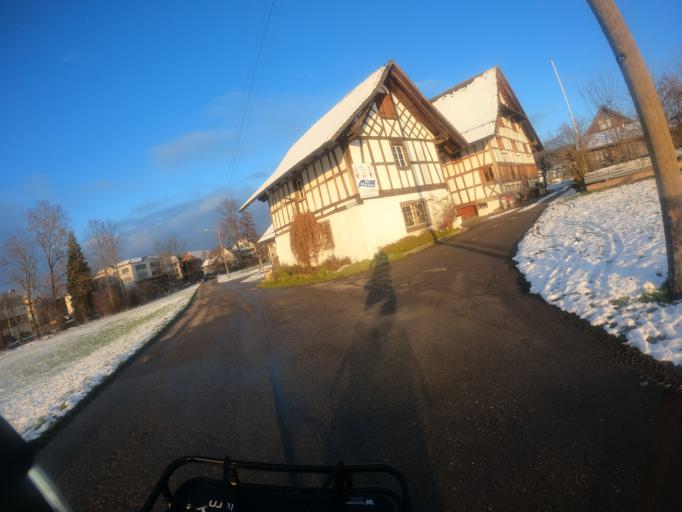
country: CH
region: Zurich
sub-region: Bezirk Affoltern
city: Affoltern / Unterdorf
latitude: 47.2878
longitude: 8.4420
